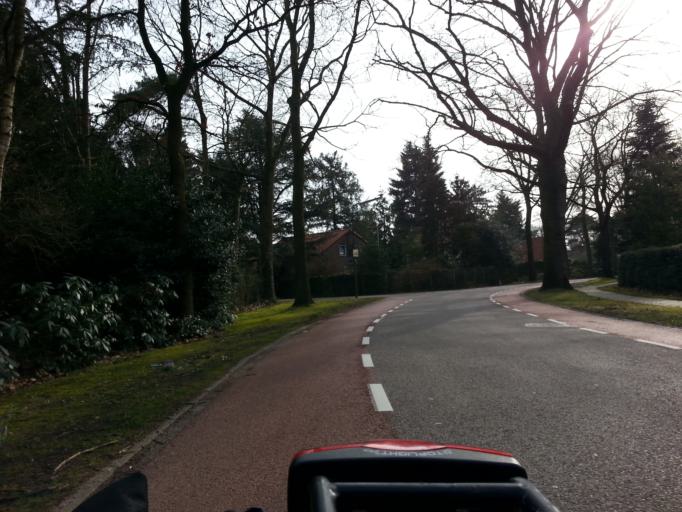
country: NL
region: Utrecht
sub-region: Gemeente Utrechtse Heuvelrug
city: Maarn
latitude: 52.0670
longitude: 5.3624
